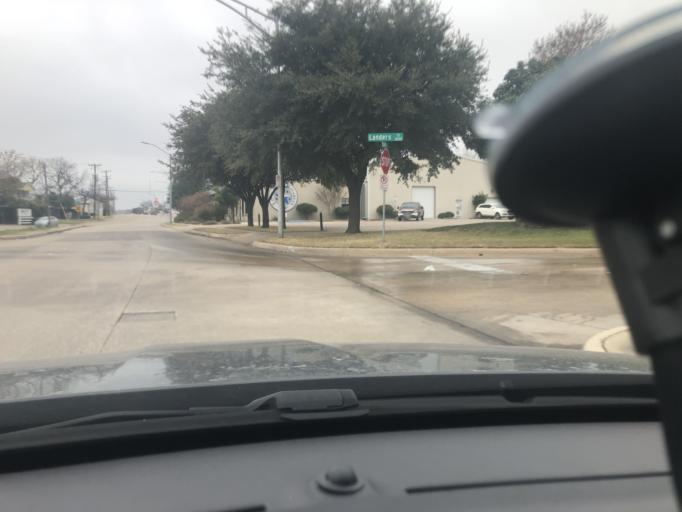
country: US
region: Texas
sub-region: Tarrant County
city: Westworth
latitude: 32.7306
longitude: -97.3717
